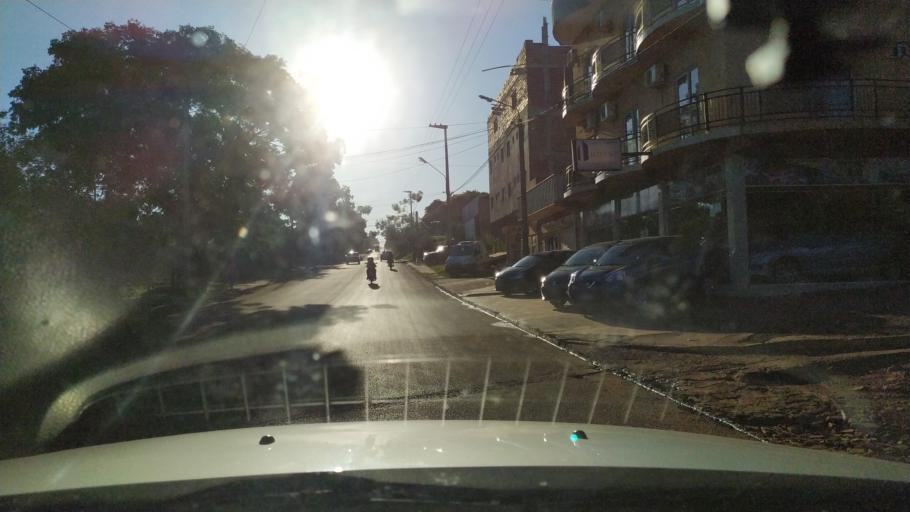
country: AR
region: Misiones
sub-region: Departamento de Eldorado
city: Eldorado
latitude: -26.4147
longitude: -54.6229
